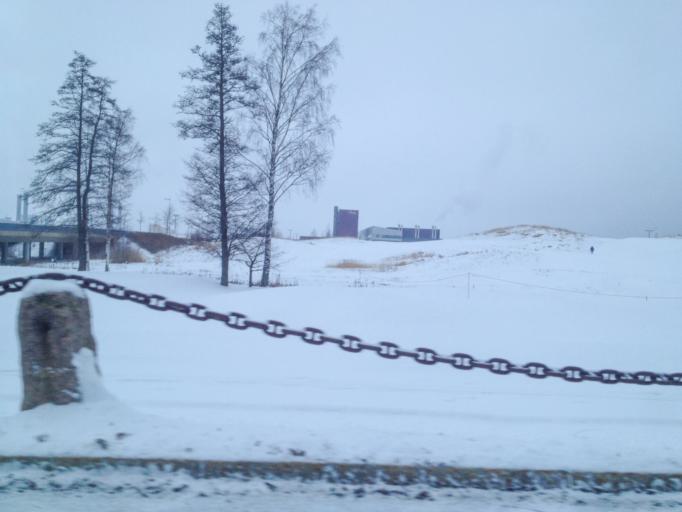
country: FI
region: Uusimaa
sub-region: Helsinki
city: Vantaa
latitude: 60.2101
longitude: 25.1642
